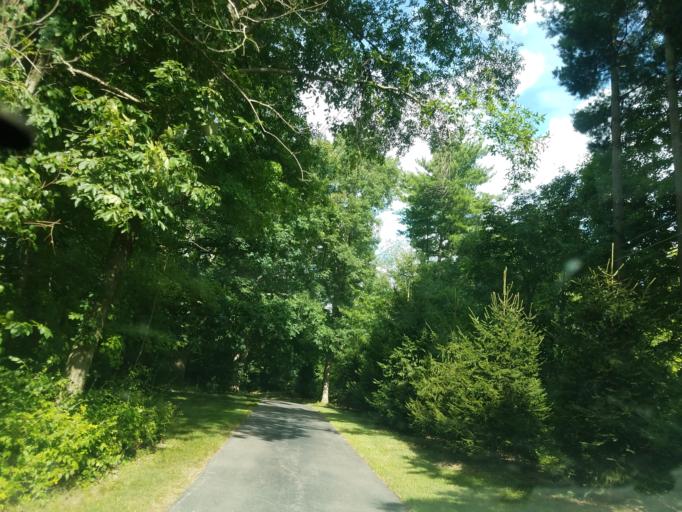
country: US
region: Ohio
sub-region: Delaware County
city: Powell
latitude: 40.1718
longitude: -83.0576
